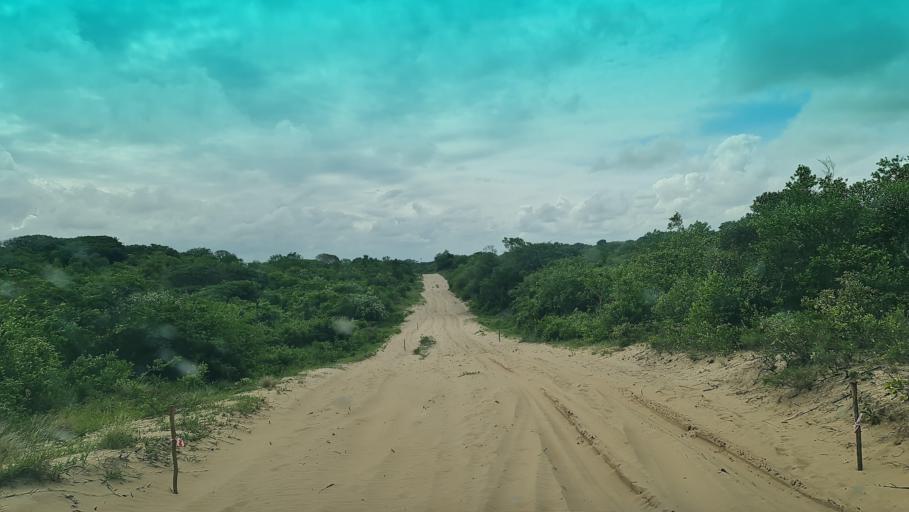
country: MZ
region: Maputo
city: Manhica
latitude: -25.4344
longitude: 32.9093
